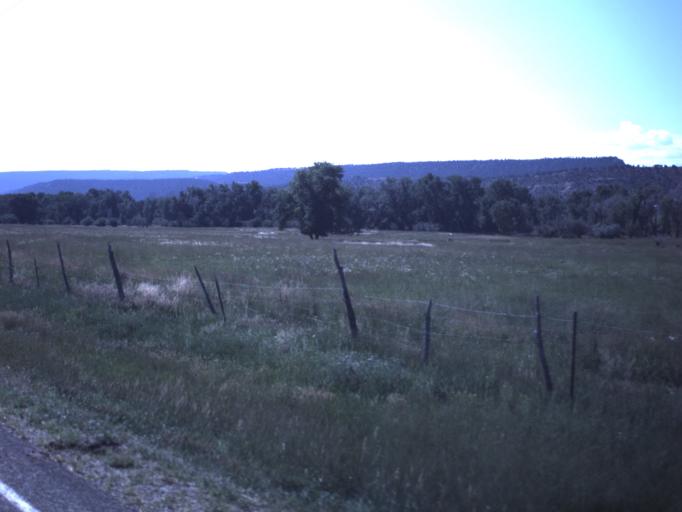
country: US
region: Utah
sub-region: Duchesne County
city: Duchesne
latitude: 40.3423
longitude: -110.6943
